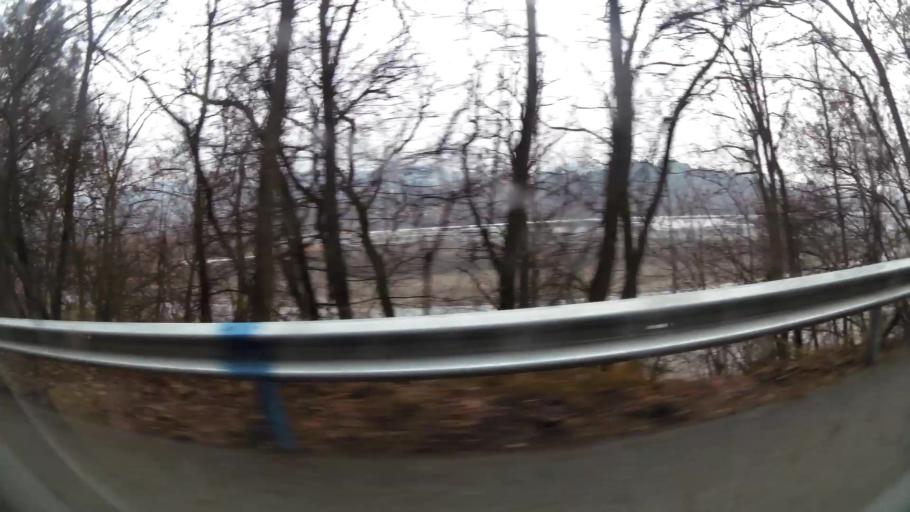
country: BG
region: Sofia-Capital
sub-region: Stolichna Obshtina
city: Sofia
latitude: 42.5910
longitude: 23.4242
